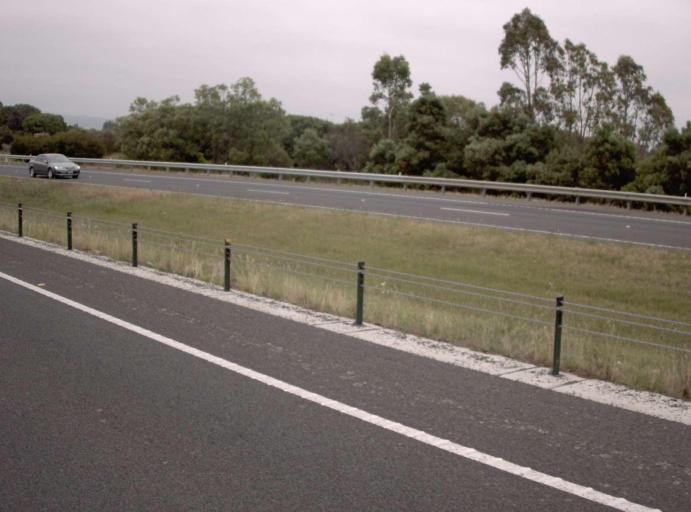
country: AU
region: Victoria
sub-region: Latrobe
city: Morwell
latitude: -38.2417
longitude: 146.4073
